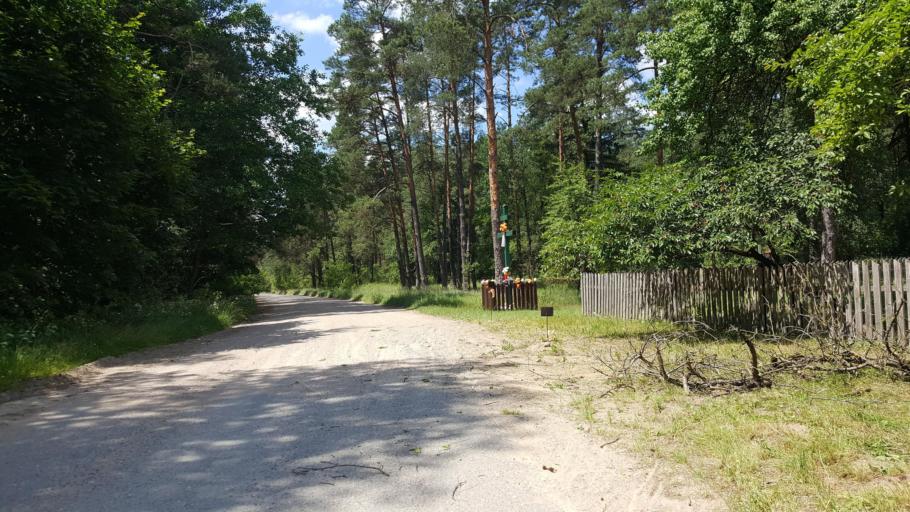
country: BY
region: Brest
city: Kamyanyuki
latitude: 52.5616
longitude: 23.7918
